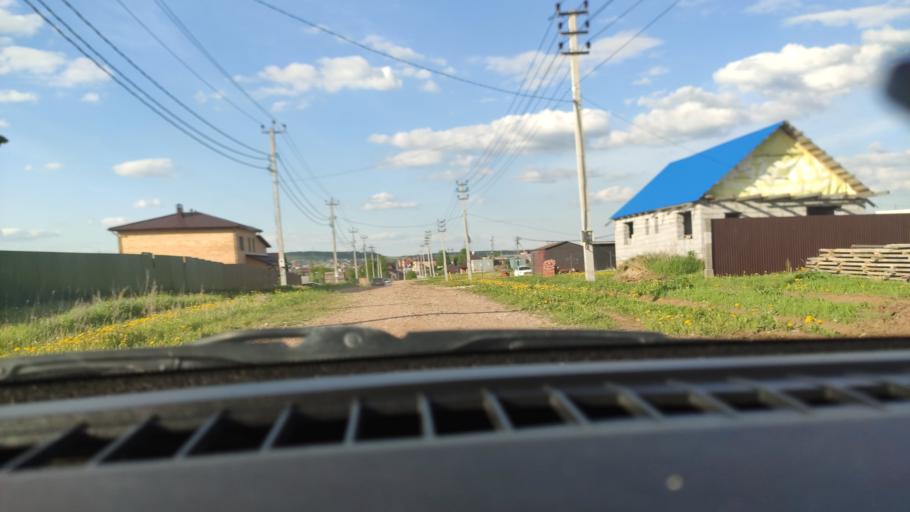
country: RU
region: Perm
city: Ferma
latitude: 57.9376
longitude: 56.3541
